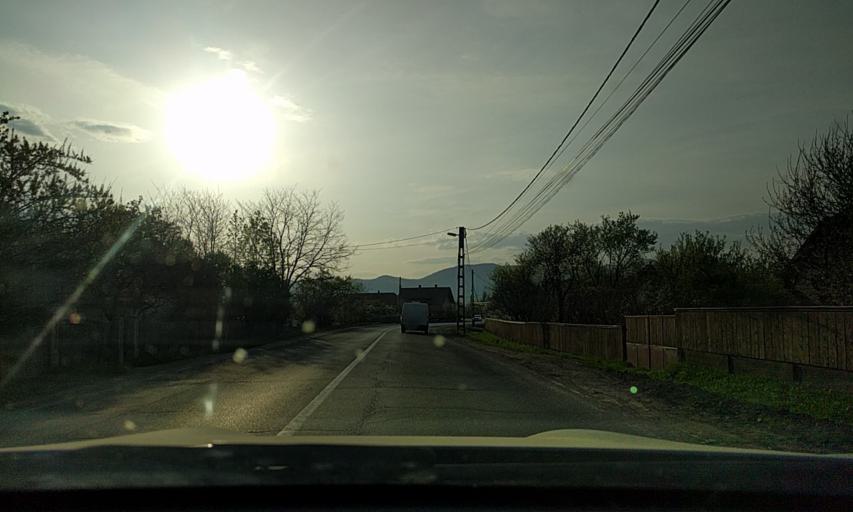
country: RO
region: Covasna
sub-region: Comuna Lemnia
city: Lemnia
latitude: 46.0450
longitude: 26.2607
